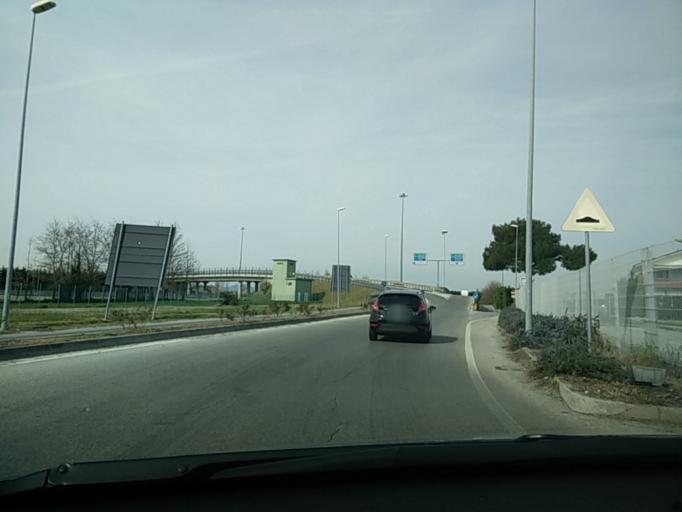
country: IT
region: Emilia-Romagna
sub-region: Provincia di Rimini
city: Rimini
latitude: 44.0687
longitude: 12.5262
